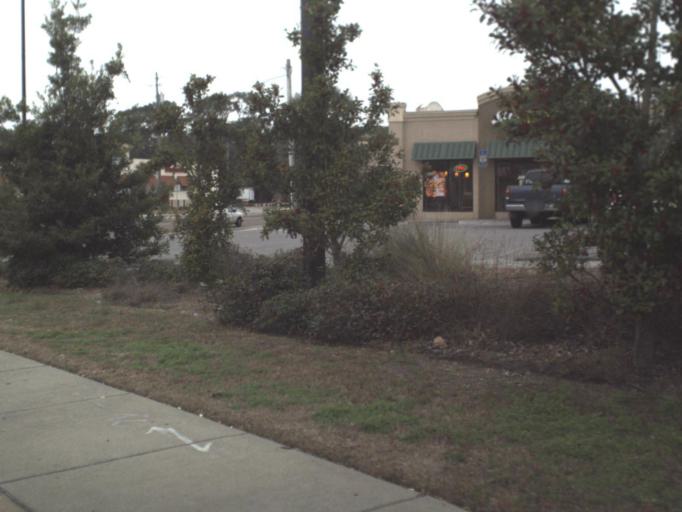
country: US
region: Florida
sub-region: Bay County
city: Panama City
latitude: 30.1573
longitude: -85.6500
